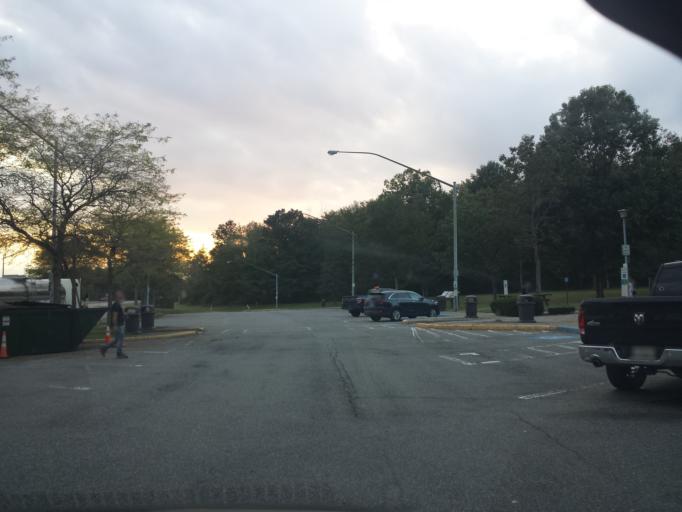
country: US
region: Pennsylvania
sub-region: Union County
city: Mifflinburg
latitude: 41.0523
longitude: -77.1583
